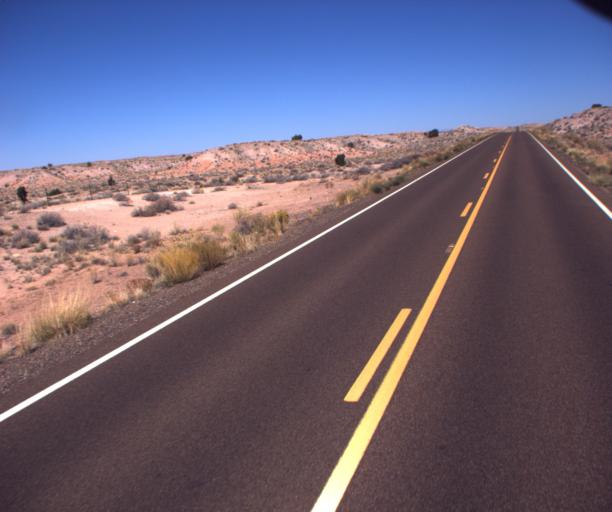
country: US
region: Arizona
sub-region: Navajo County
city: Dilkon
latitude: 35.1900
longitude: -110.4421
